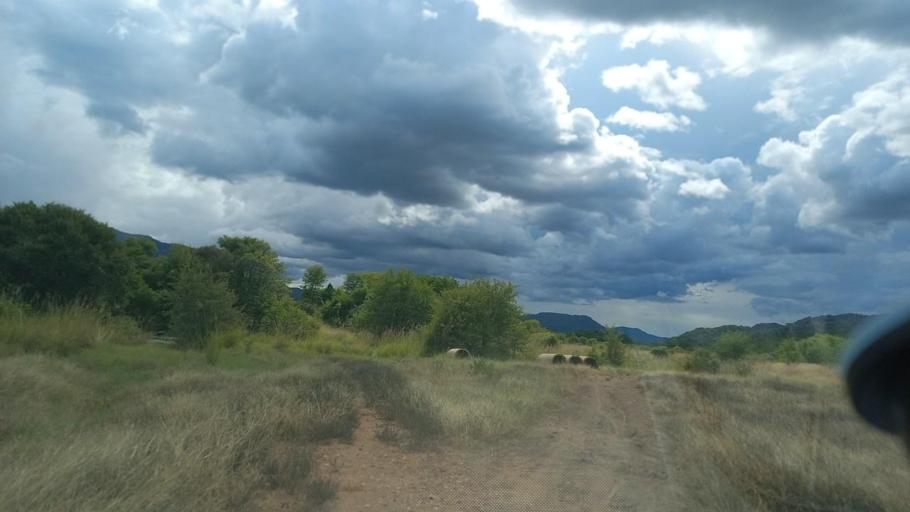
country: ZM
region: Lusaka
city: Luangwa
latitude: -15.6518
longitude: 30.3479
